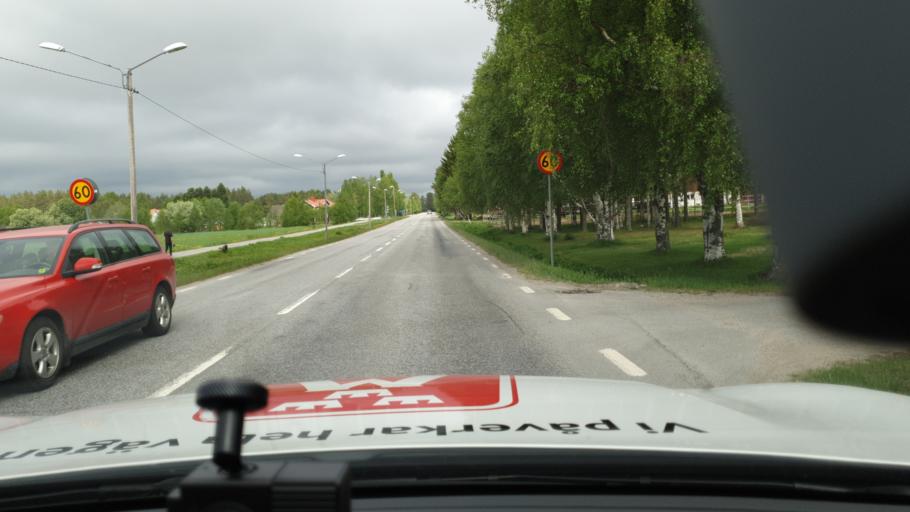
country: SE
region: Vaesterbotten
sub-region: Umea Kommun
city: Roback
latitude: 63.9396
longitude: 20.1597
